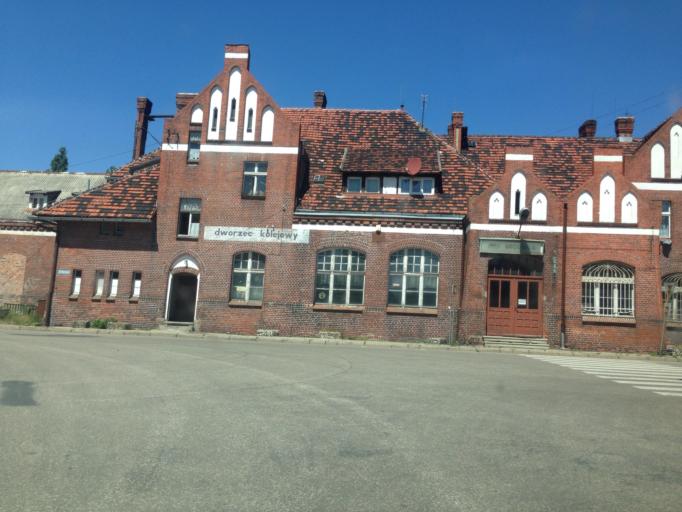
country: PL
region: Kujawsko-Pomorskie
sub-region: Powiat brodnicki
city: Brodnica
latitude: 53.2629
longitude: 19.4058
